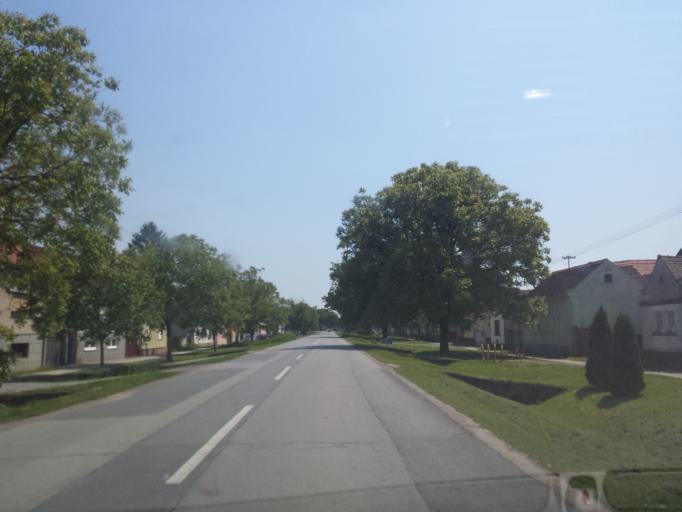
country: HR
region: Brodsko-Posavska
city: Luzani
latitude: 45.1682
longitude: 17.6975
